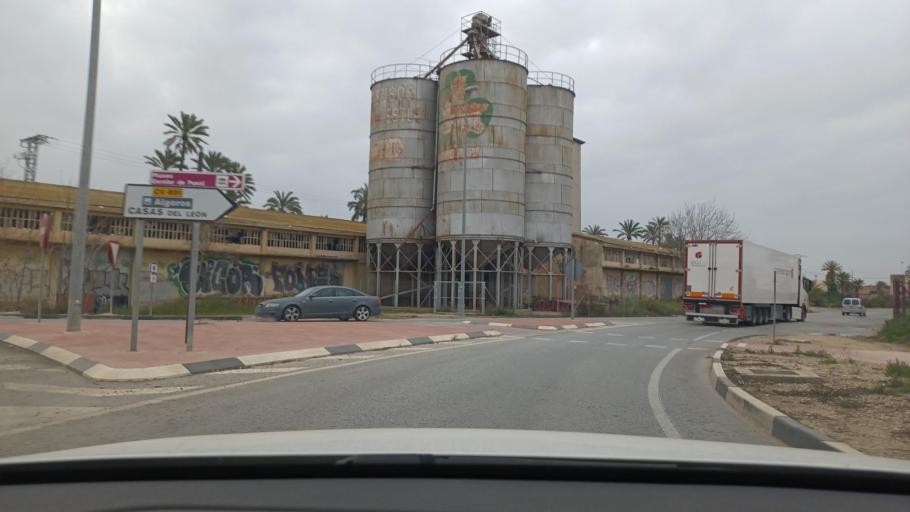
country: ES
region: Valencia
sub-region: Provincia de Alicante
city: Elche
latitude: 38.2495
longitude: -0.7047
